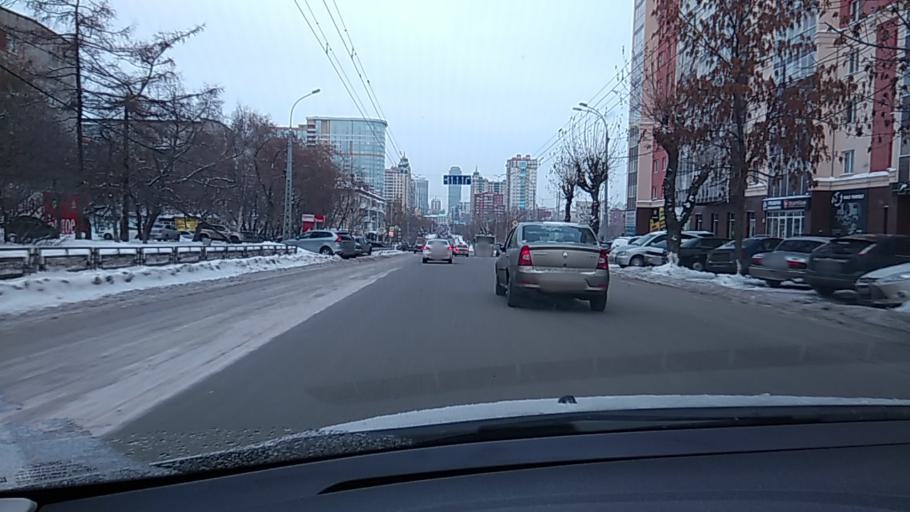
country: RU
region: Sverdlovsk
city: Yekaterinburg
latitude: 56.8156
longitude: 60.6210
